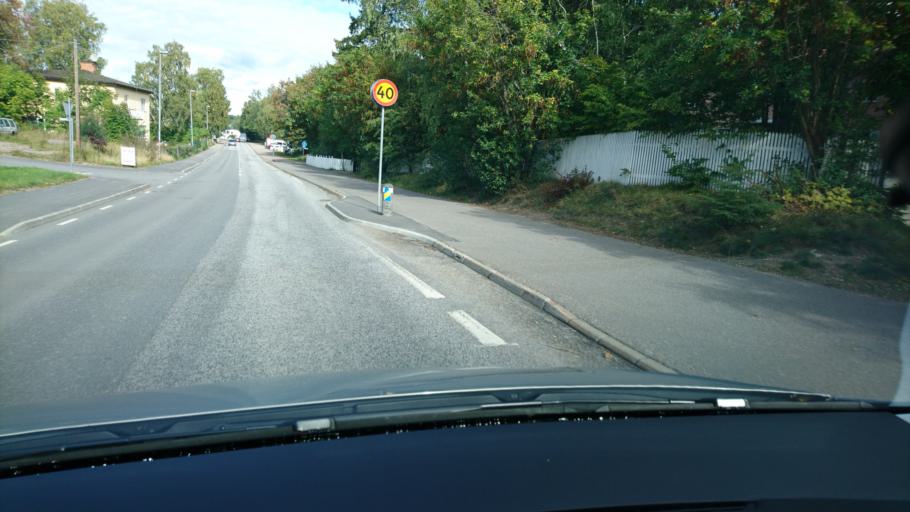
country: SE
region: Soedermanland
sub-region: Strangnas Kommun
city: Stallarholmen
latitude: 59.3579
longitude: 17.2061
